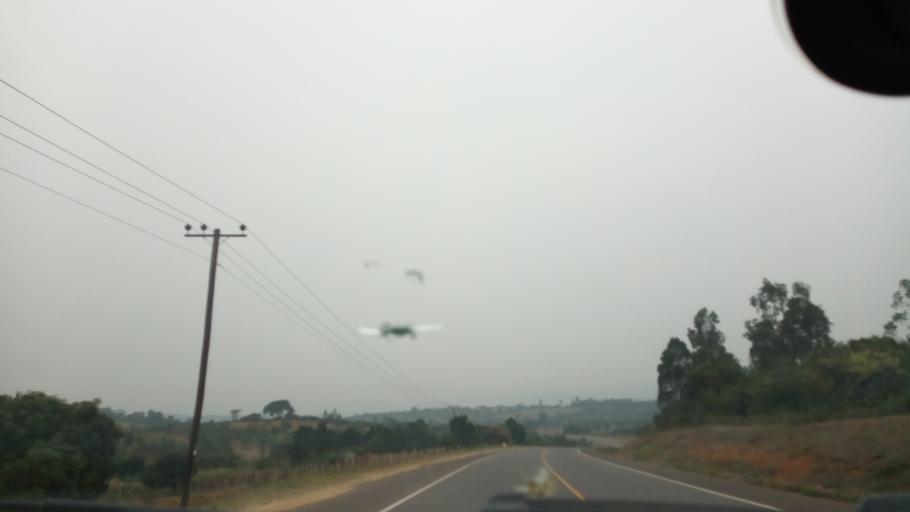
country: UG
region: Western Region
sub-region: Mbarara District
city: Mbarara
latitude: -0.7060
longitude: 30.7093
